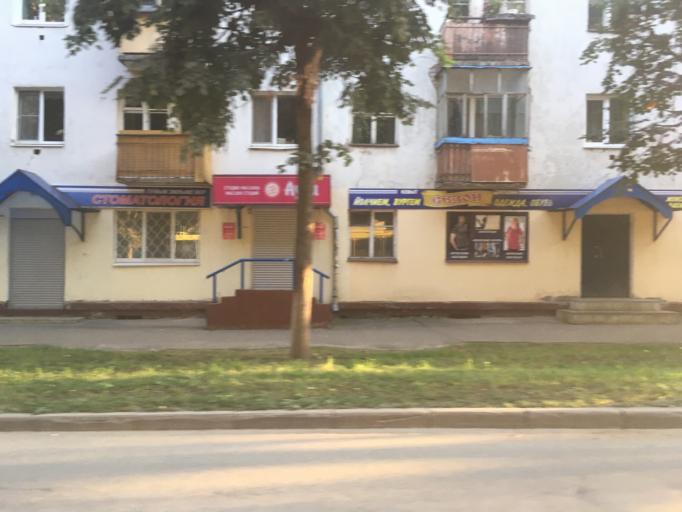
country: RU
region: Mariy-El
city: Yoshkar-Ola
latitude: 56.6470
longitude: 47.8858
